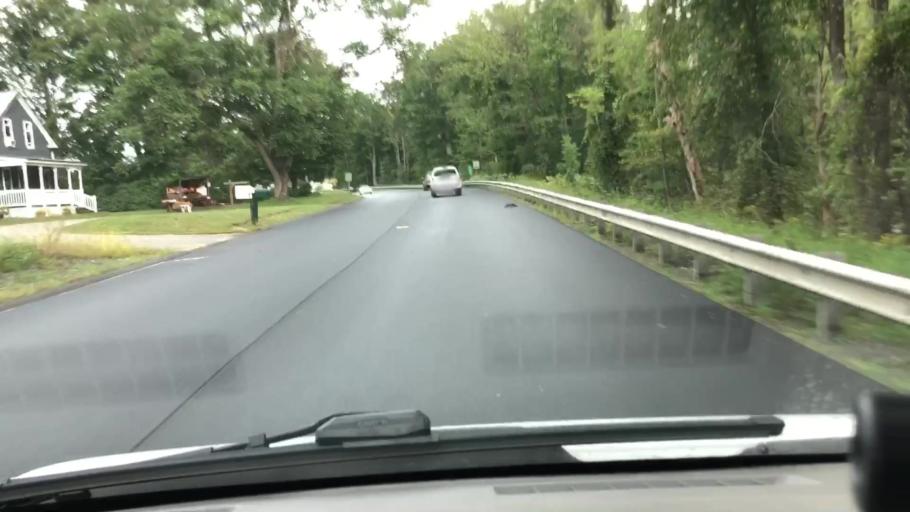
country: US
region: Massachusetts
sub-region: Franklin County
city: Charlemont
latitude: 42.6173
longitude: -72.8355
